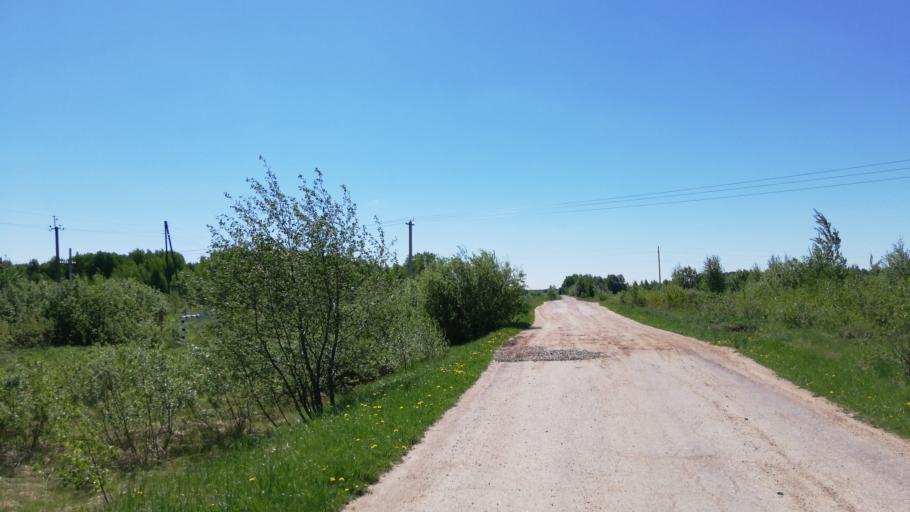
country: RU
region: Ivanovo
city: Pistsovo
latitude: 57.1255
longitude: 40.6011
